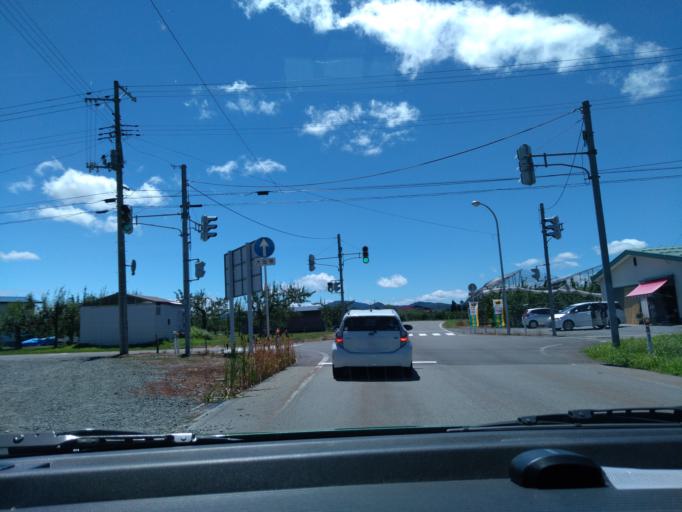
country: JP
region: Akita
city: Yuzawa
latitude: 39.2138
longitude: 140.5661
